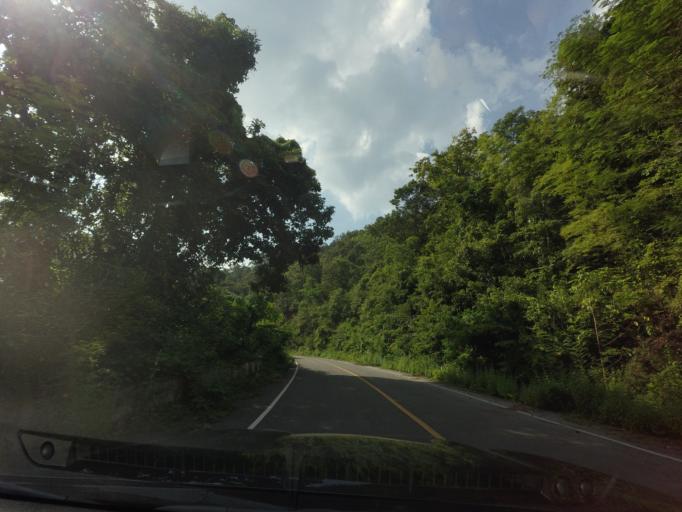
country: TH
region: Nan
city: Na Noi
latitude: 18.3128
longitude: 100.8978
